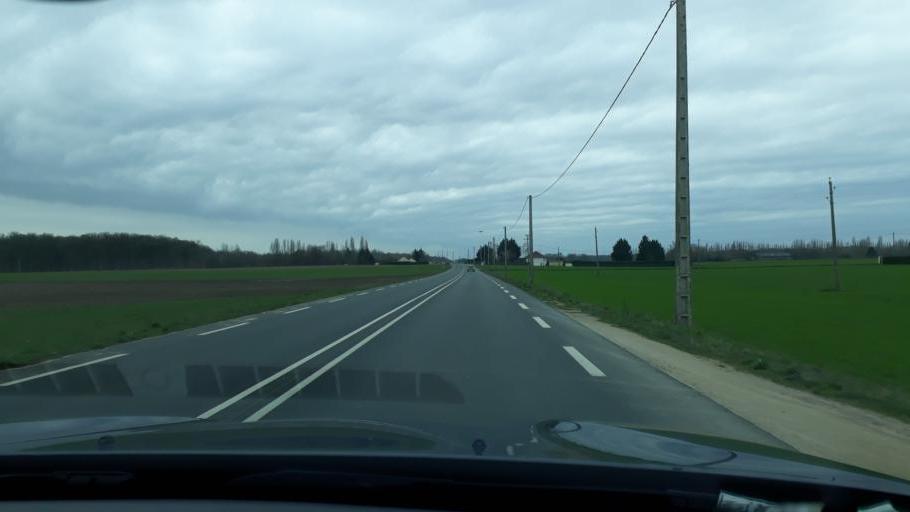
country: FR
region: Centre
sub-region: Departement du Loiret
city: Chanteau
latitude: 48.0346
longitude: 1.9766
